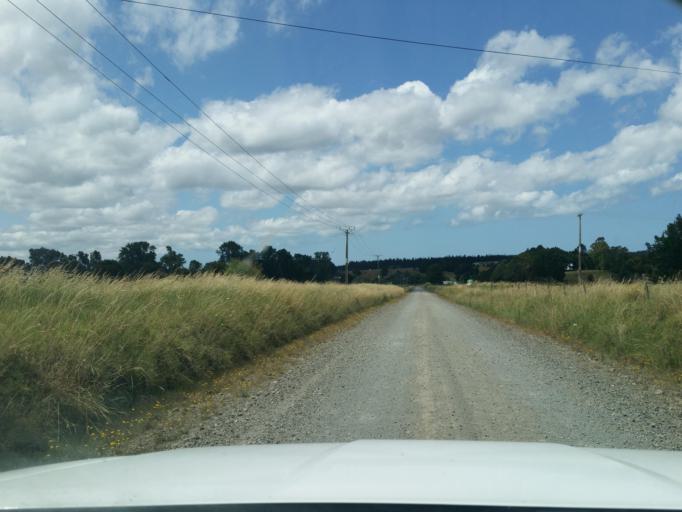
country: NZ
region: Northland
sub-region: Kaipara District
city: Dargaville
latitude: -35.8009
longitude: 173.7314
